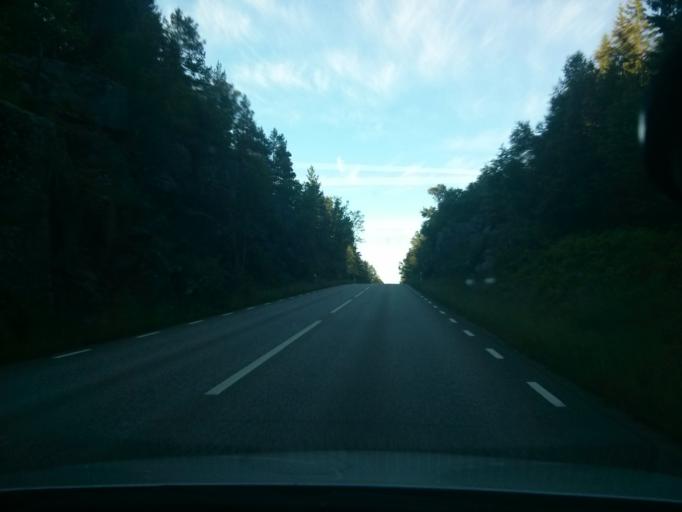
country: SE
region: Blekinge
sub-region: Ronneby Kommun
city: Brakne-Hoby
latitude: 56.3315
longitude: 15.1725
